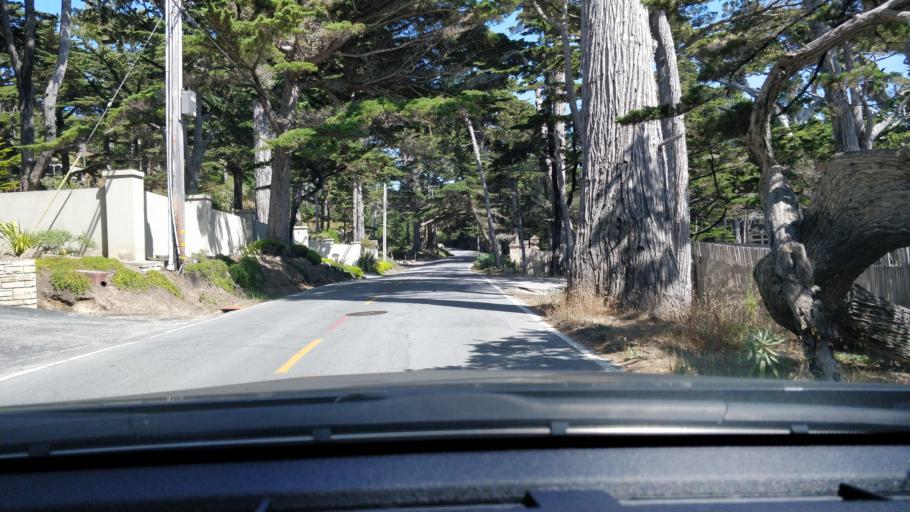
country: US
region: California
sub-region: Monterey County
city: Del Monte Forest
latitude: 36.5692
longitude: -121.9641
